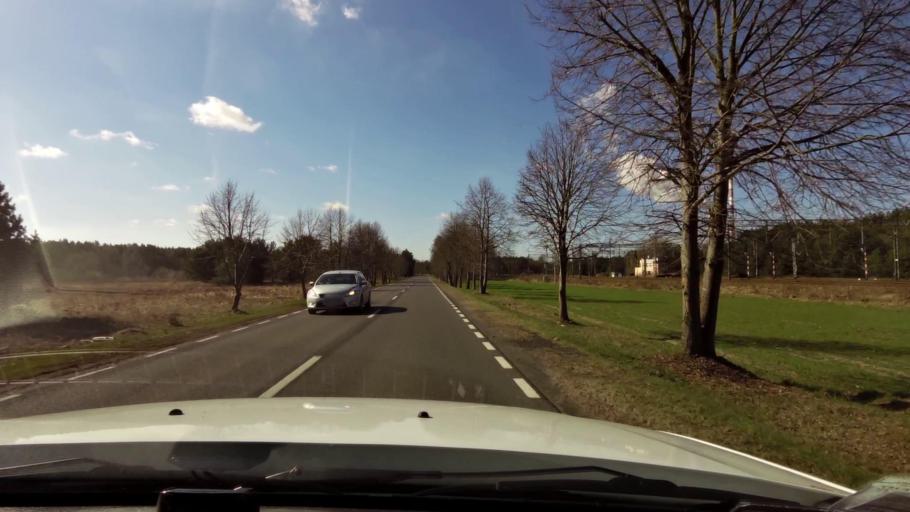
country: PL
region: West Pomeranian Voivodeship
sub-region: Powiat gryfinski
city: Gryfino
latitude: 53.2150
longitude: 14.4841
